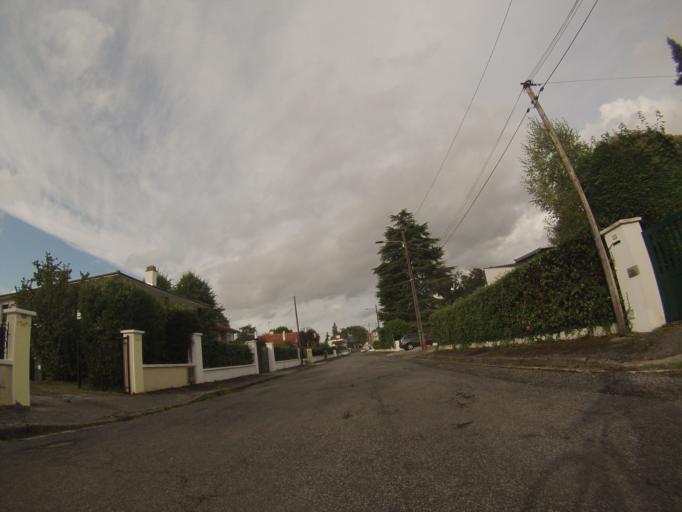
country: FR
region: Aquitaine
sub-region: Departement des Pyrenees-Atlantiques
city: Gelos
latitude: 43.2824
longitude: -0.3749
